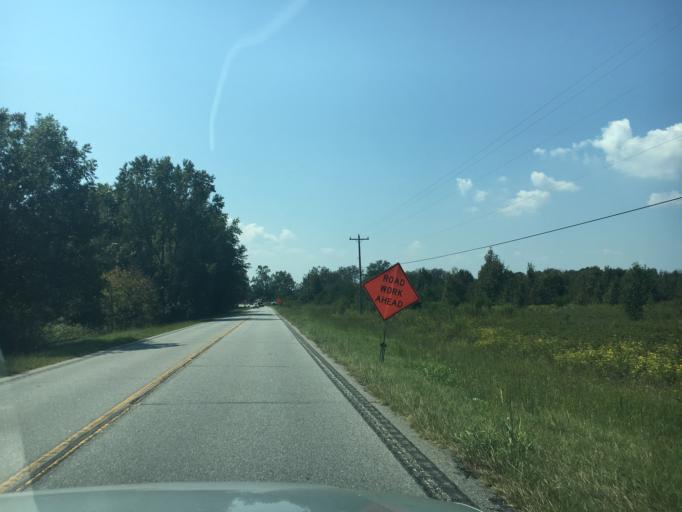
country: US
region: South Carolina
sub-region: Anderson County
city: Centerville
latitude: 34.4550
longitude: -82.7914
